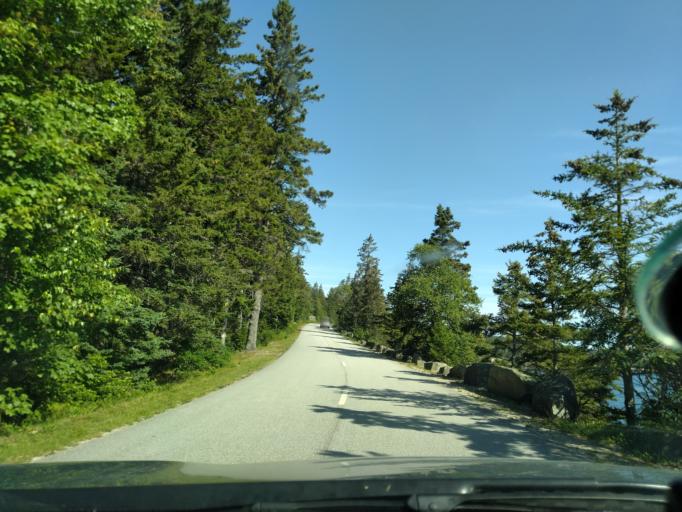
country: US
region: Maine
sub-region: Hancock County
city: Gouldsboro
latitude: 44.3501
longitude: -68.0461
